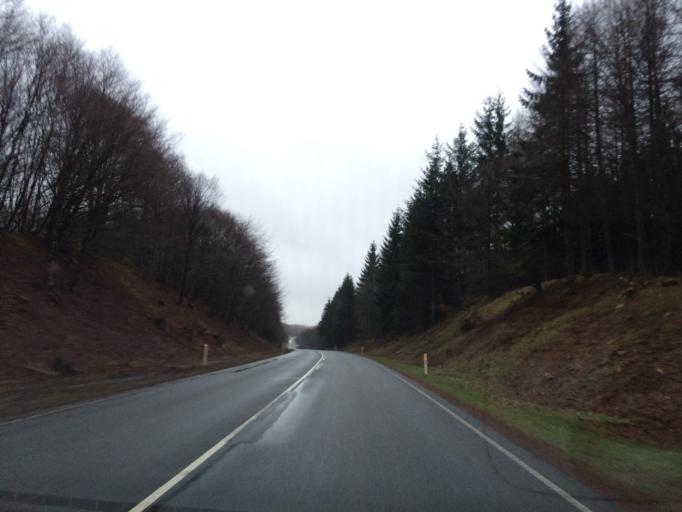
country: DK
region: North Denmark
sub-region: Mariagerfjord Kommune
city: Arden
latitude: 56.8022
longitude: 9.8172
